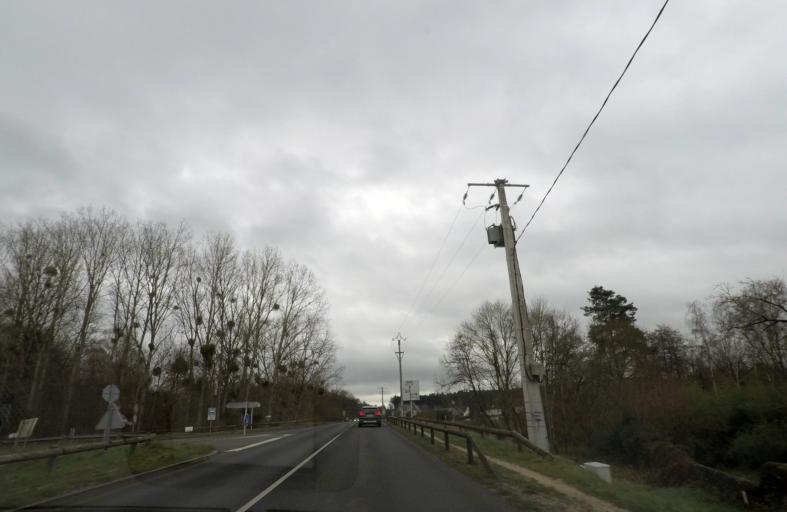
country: FR
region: Centre
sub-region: Departement du Loir-et-Cher
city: Cellettes
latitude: 47.5329
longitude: 1.4196
